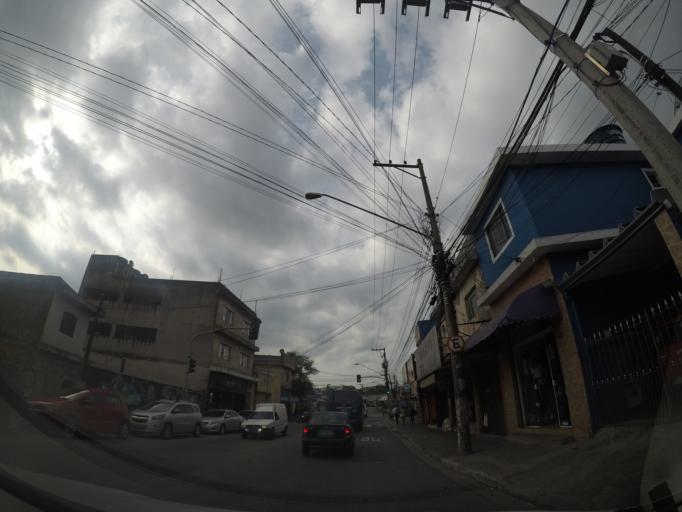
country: BR
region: Sao Paulo
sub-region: Guarulhos
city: Guarulhos
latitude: -23.4256
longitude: -46.5041
